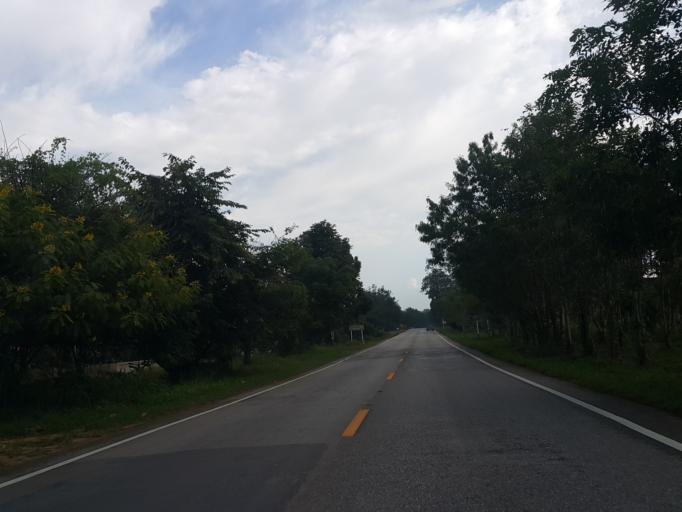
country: TH
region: Chiang Mai
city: Phrao
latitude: 19.2783
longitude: 99.1893
